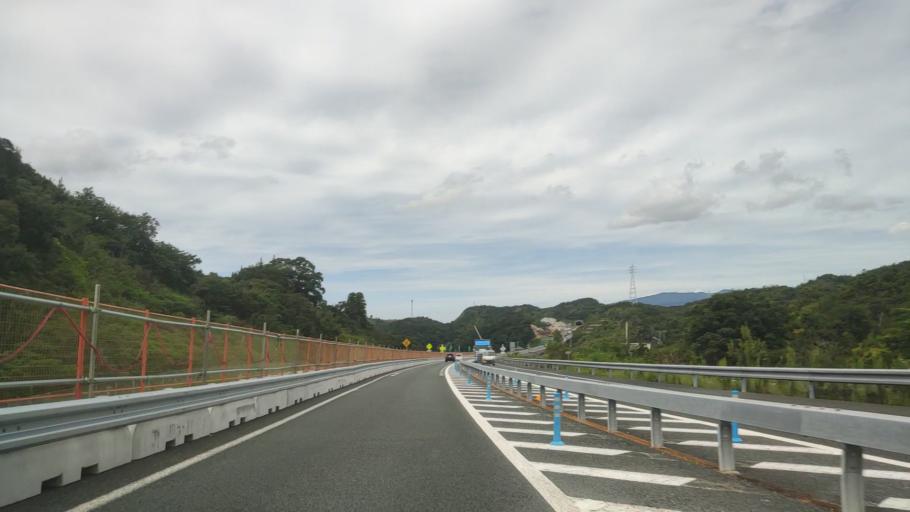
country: JP
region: Wakayama
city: Gobo
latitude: 33.8657
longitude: 135.1912
